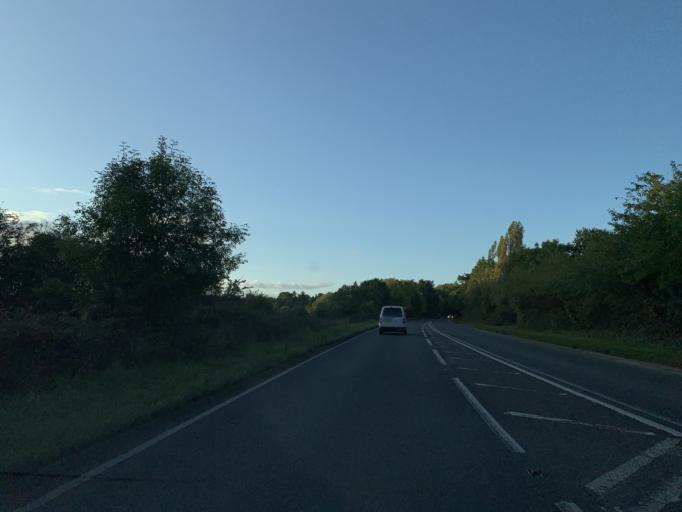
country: GB
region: England
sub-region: Wiltshire
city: Whiteparish
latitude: 50.9820
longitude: -1.6382
